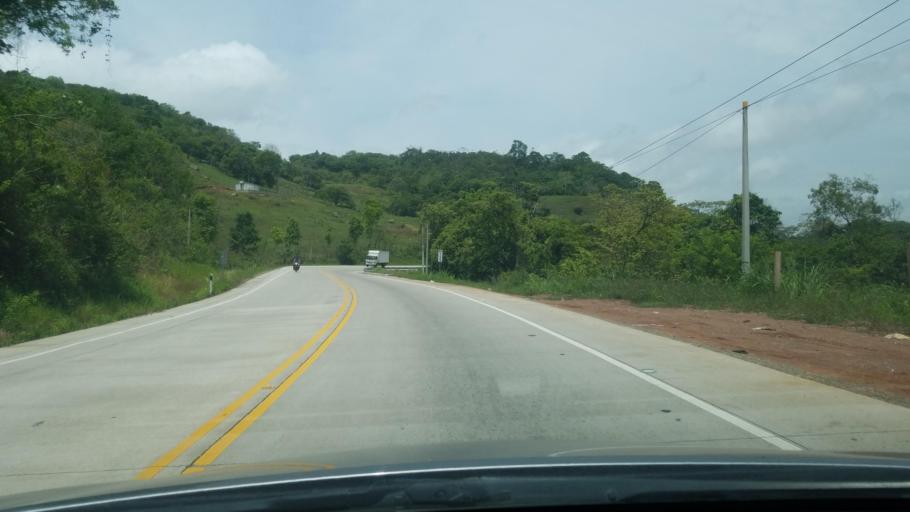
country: HN
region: Copan
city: Agua Caliente
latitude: 14.8611
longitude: -88.7902
